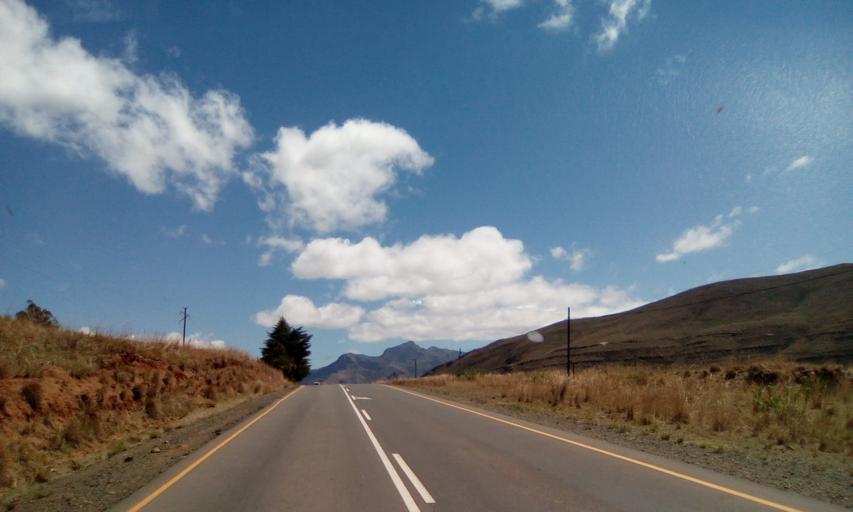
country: LS
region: Qacha's Nek
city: Qacha's Nek
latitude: -30.0946
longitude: 28.6471
